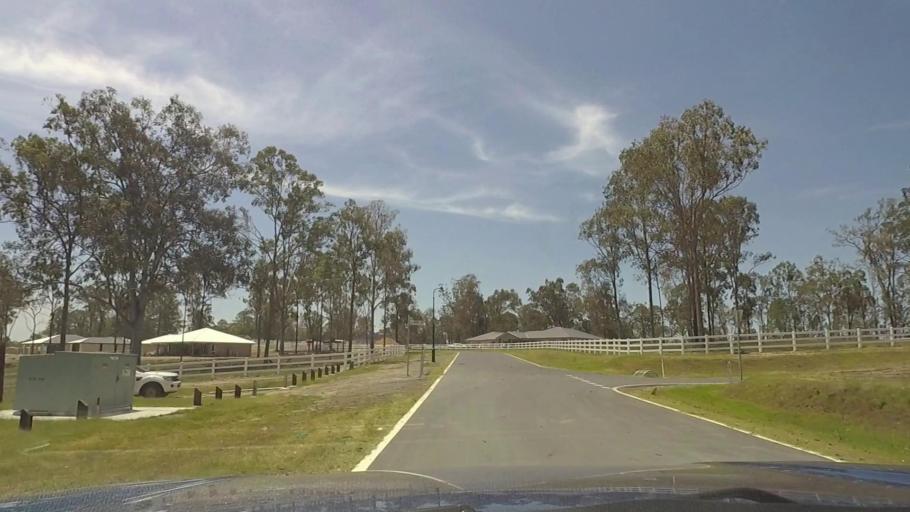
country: AU
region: Queensland
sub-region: Logan
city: North Maclean
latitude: -27.7784
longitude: 153.0366
